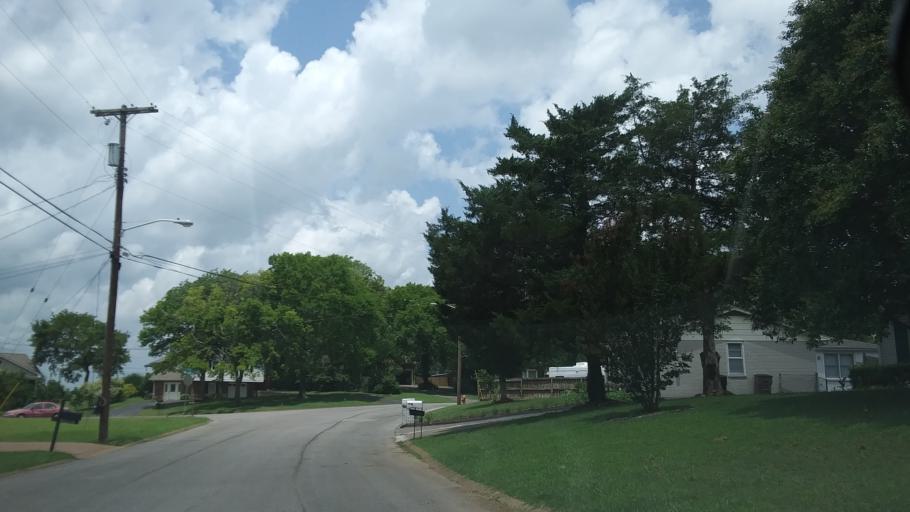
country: US
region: Tennessee
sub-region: Davidson County
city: Belle Meade
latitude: 36.1381
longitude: -86.8934
